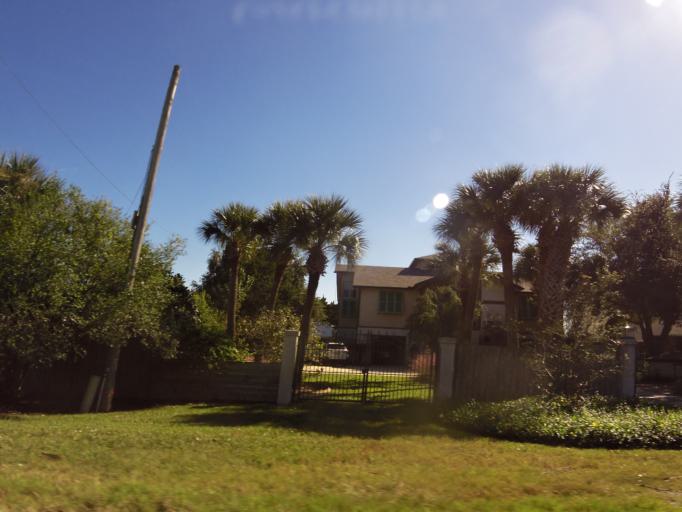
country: US
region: Florida
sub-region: Duval County
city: Atlantic Beach
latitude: 30.3849
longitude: -81.4486
